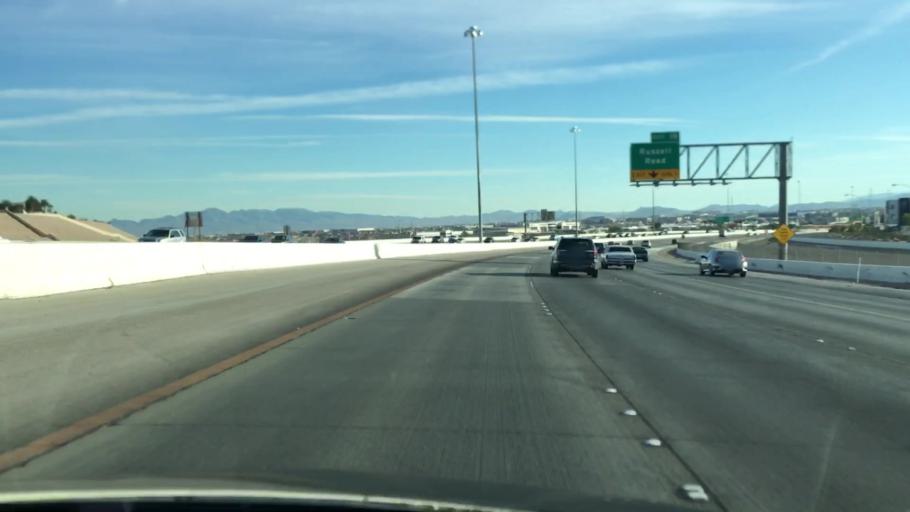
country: US
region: Nevada
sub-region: Clark County
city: Summerlin South
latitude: 36.0959
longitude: -115.2908
